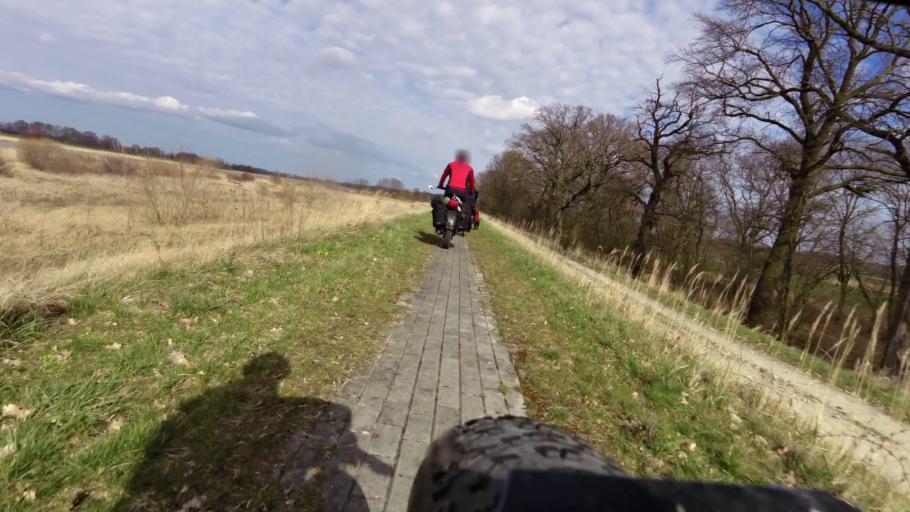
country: PL
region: Lubusz
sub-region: Powiat slubicki
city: Gorzyca
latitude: 52.4772
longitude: 14.6191
